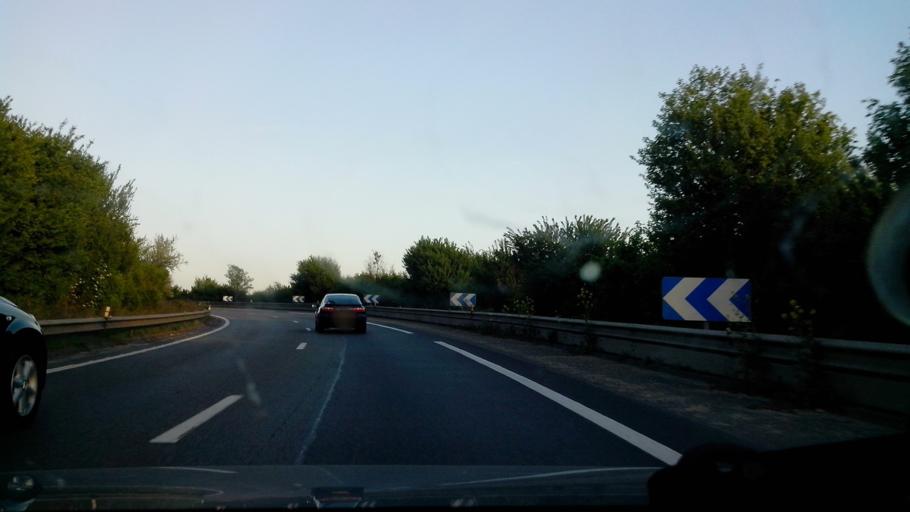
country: FR
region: Ile-de-France
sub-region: Departement de Seine-et-Marne
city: Lieusaint
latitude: 48.6307
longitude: 2.5340
